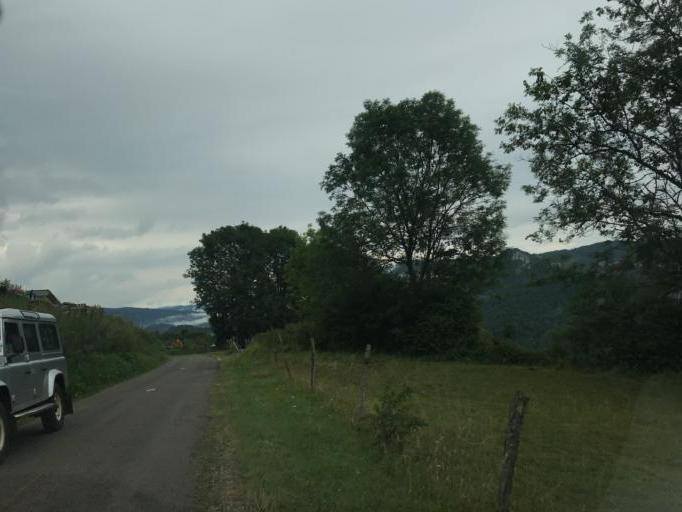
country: FR
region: Franche-Comte
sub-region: Departement du Jura
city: Lavans-les-Saint-Claude
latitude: 46.3301
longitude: 5.7525
